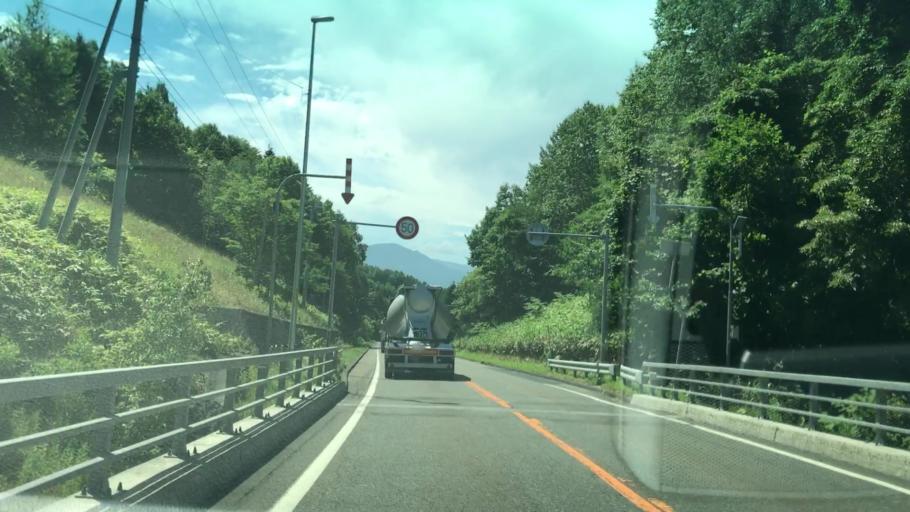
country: JP
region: Hokkaido
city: Shimo-furano
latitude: 42.8983
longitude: 142.4357
